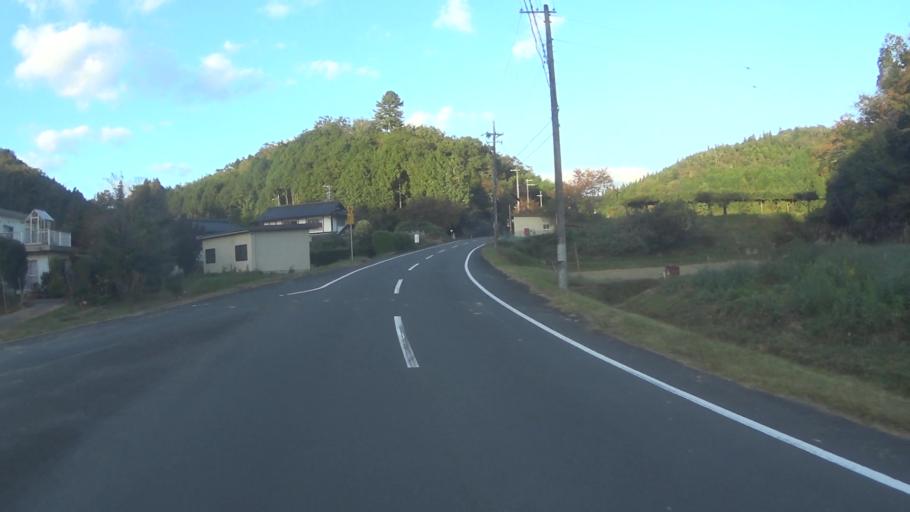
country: JP
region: Kyoto
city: Ayabe
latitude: 35.2547
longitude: 135.2115
